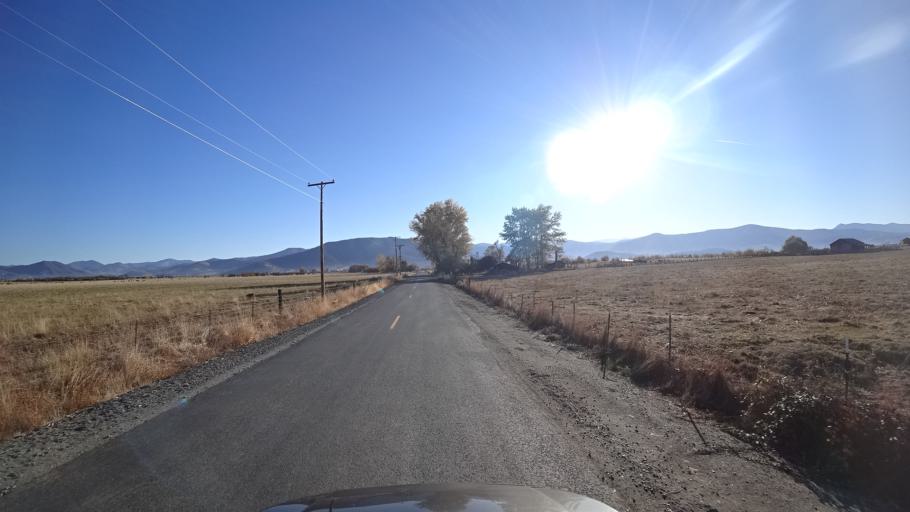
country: US
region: California
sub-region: Siskiyou County
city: Yreka
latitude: 41.5130
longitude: -122.8837
